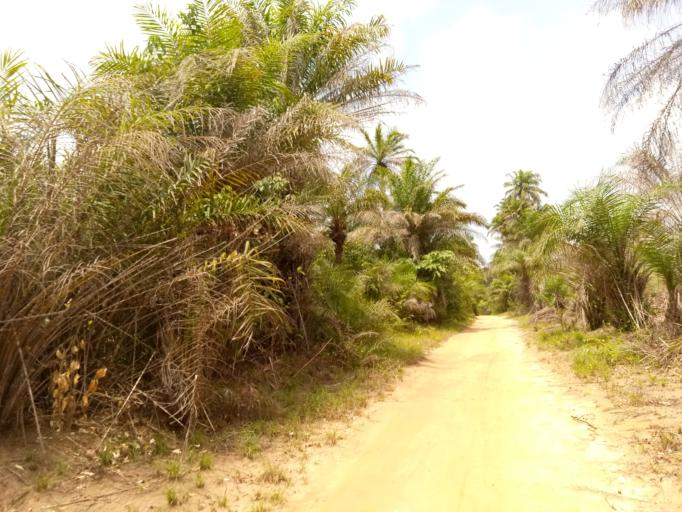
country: SL
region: Western Area
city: Waterloo
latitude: 8.4092
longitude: -13.0208
